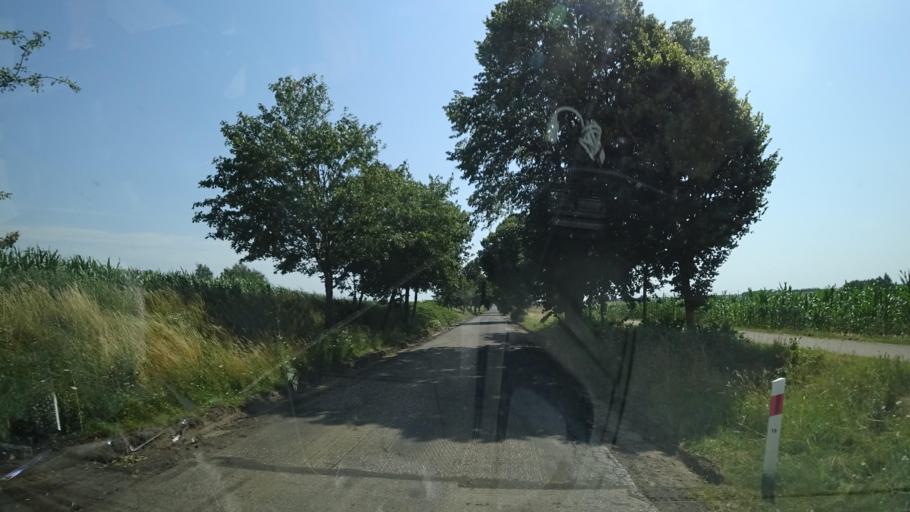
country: PL
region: Pomeranian Voivodeship
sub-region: Powiat chojnicki
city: Brusy
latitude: 53.8770
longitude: 17.6541
